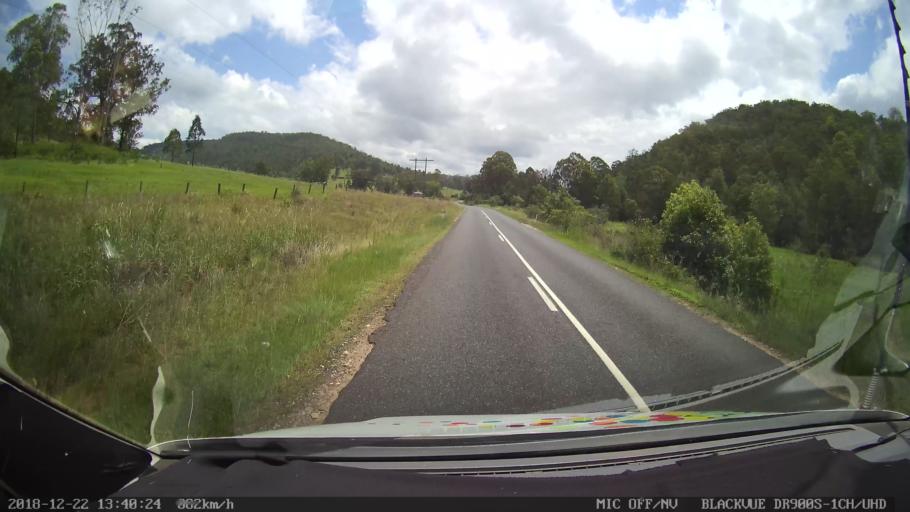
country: AU
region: New South Wales
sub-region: Clarence Valley
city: Coutts Crossing
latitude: -29.9180
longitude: 152.7772
